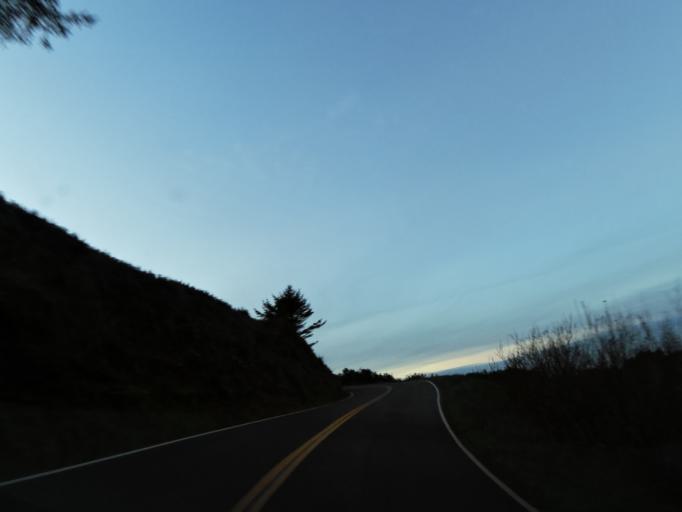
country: US
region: California
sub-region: Mendocino County
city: Fort Bragg
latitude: 39.3588
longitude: -123.8170
